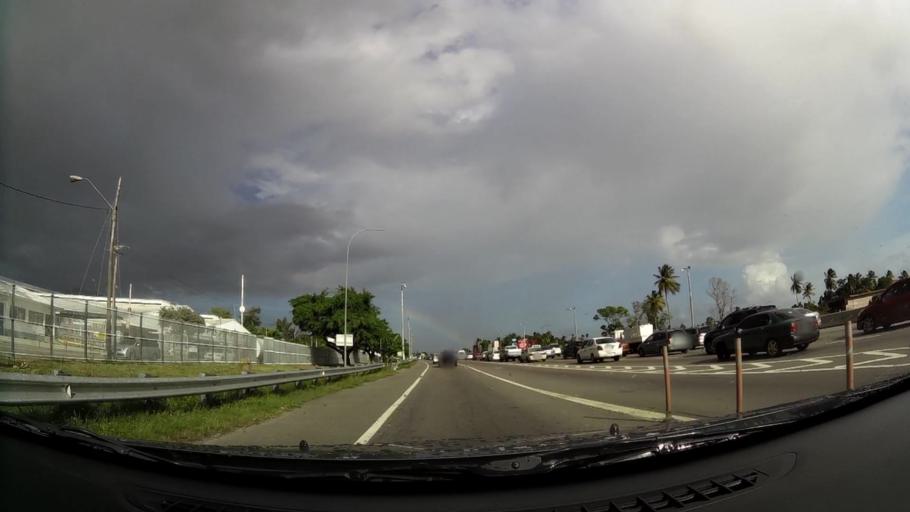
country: TT
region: Tunapuna/Piarco
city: Tunapuna
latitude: 10.6331
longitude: -61.4286
